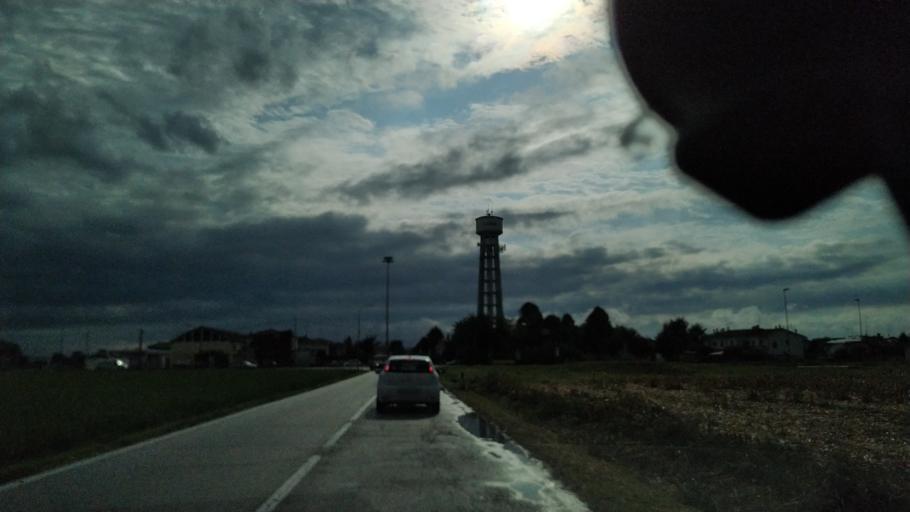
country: IT
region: Emilia-Romagna
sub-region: Provincia di Ferrara
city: San Carlo
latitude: 44.8027
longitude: 11.4168
